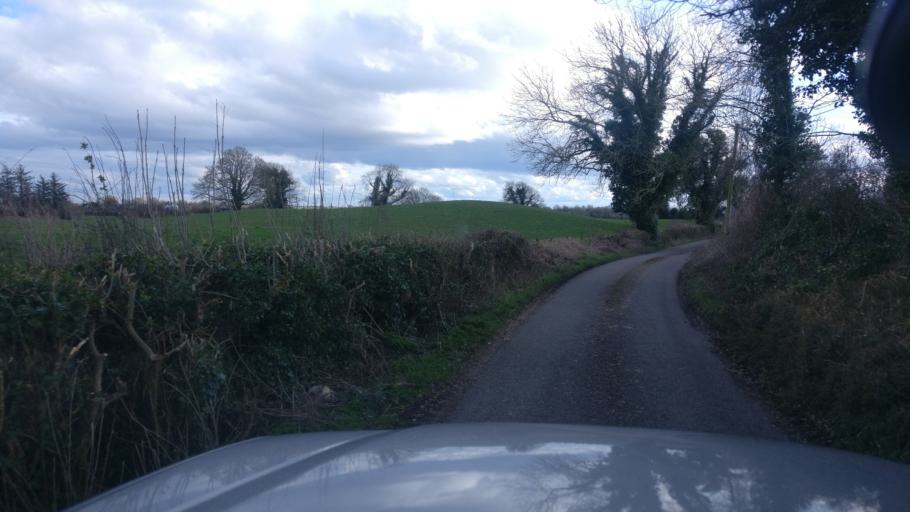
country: IE
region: Connaught
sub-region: County Galway
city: Loughrea
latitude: 53.2022
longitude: -8.4311
